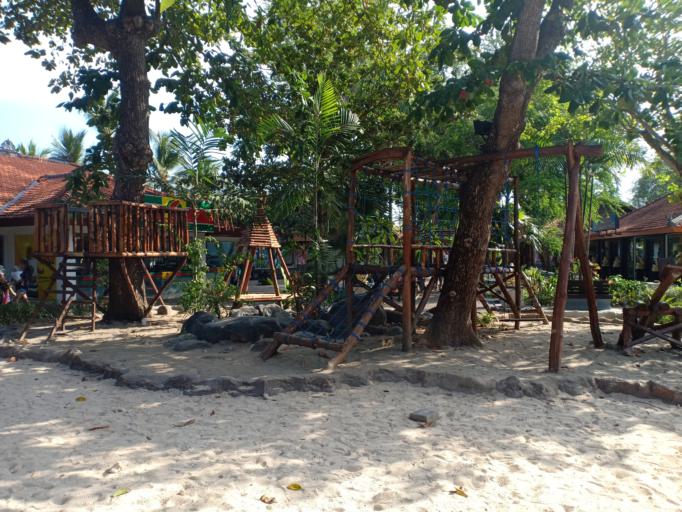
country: ID
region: Bali
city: Bualu
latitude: -8.8013
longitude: 115.2337
